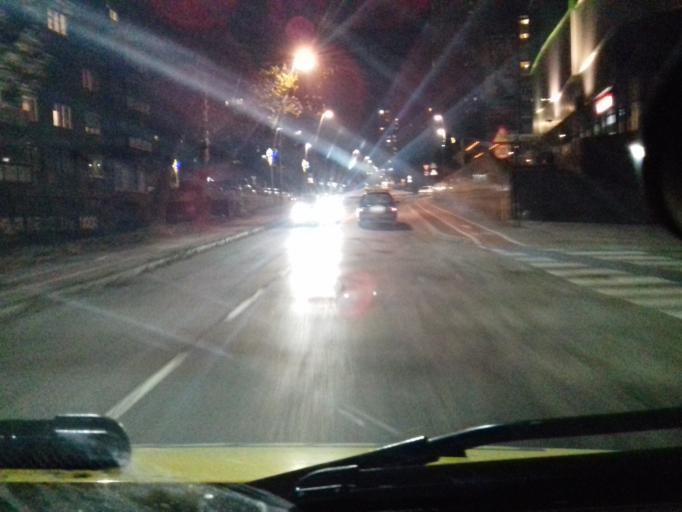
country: BA
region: Federation of Bosnia and Herzegovina
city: Zenica
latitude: 44.1990
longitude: 17.9131
